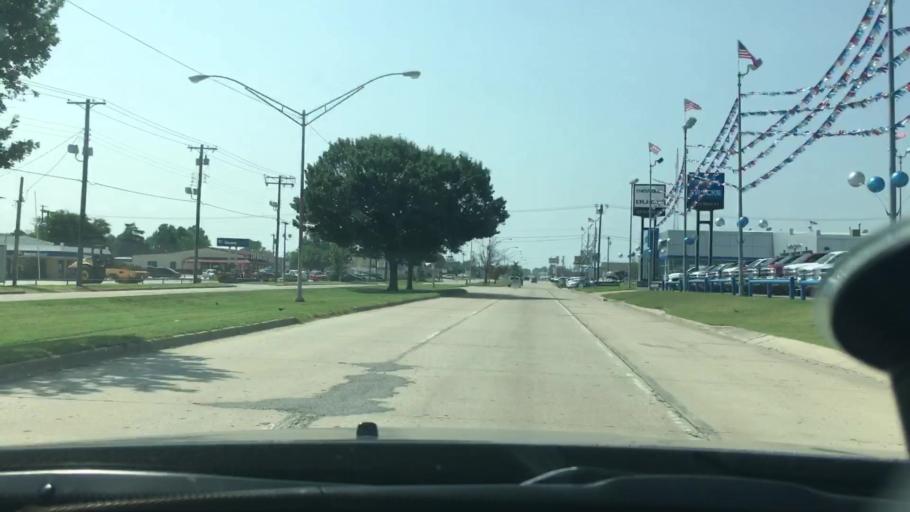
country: US
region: Oklahoma
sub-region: Pontotoc County
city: Ada
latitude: 34.7883
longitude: -96.6788
